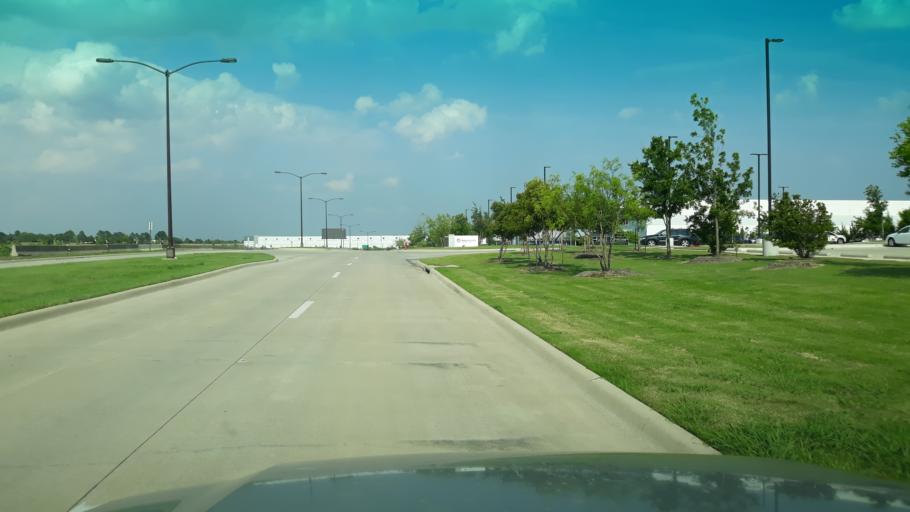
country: US
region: Texas
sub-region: Tarrant County
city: Euless
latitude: 32.8703
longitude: -97.0235
